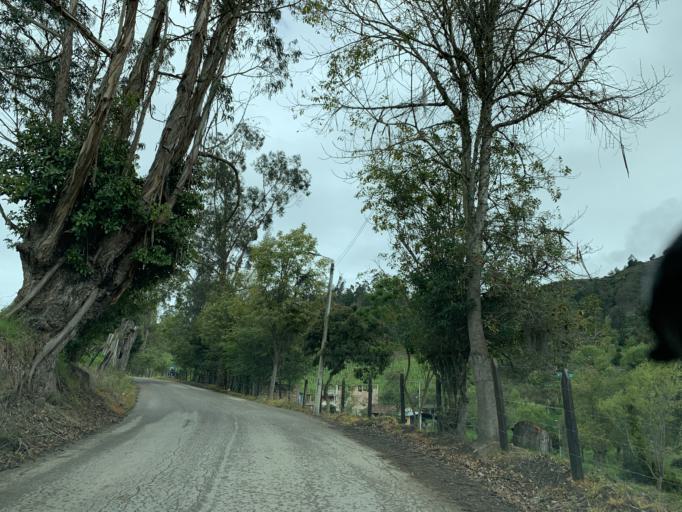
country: CO
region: Boyaca
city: Tibana
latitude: 5.3146
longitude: -73.4007
